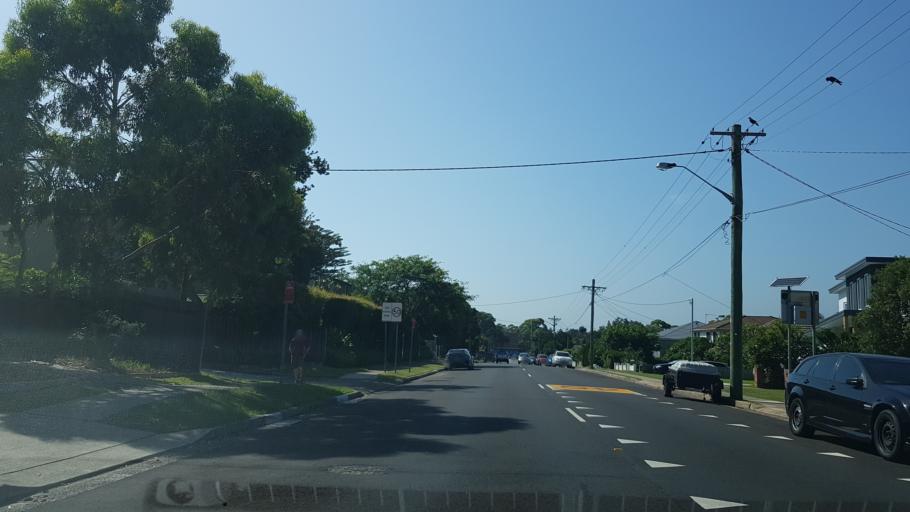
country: AU
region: New South Wales
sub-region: Warringah
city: Dee Why
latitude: -33.7422
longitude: 151.2919
